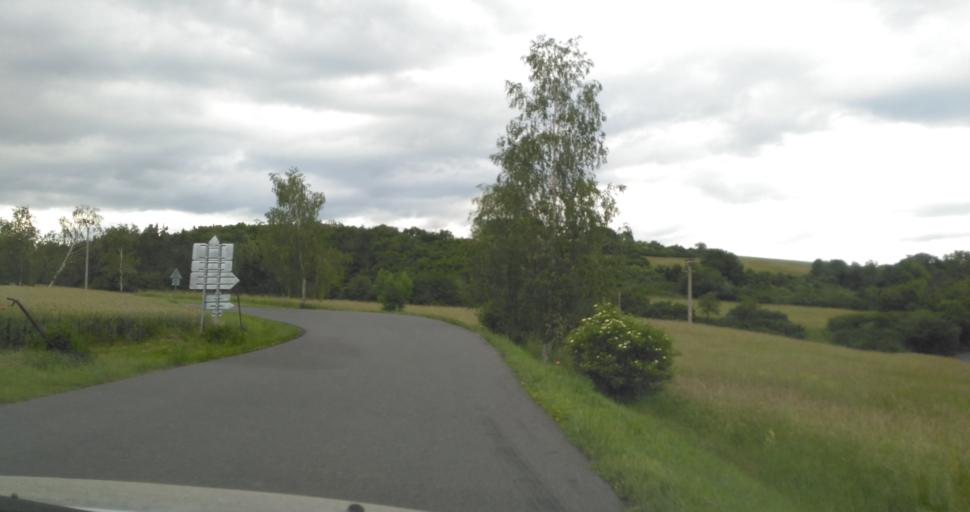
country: CZ
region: Central Bohemia
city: Zebrak
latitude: 49.8989
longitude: 13.8888
